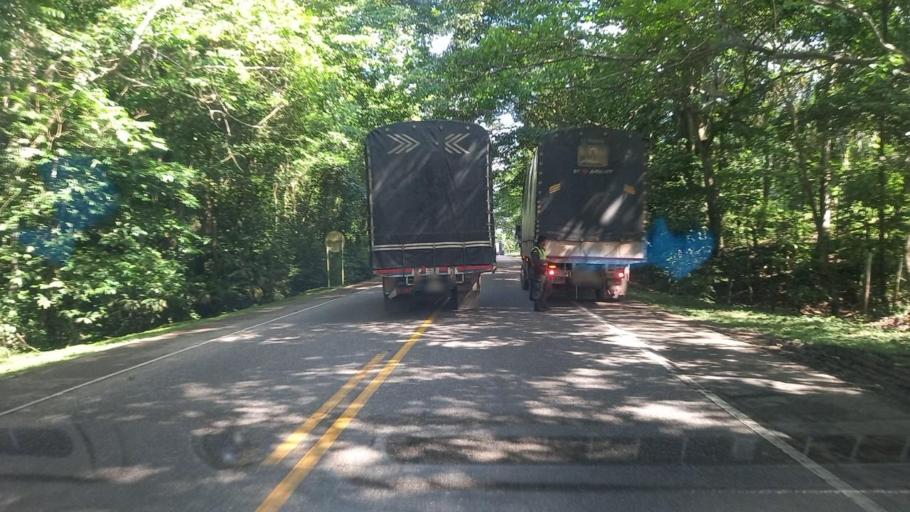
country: CO
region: Santander
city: Barrancabermeja
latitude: 6.9757
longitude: -73.6990
